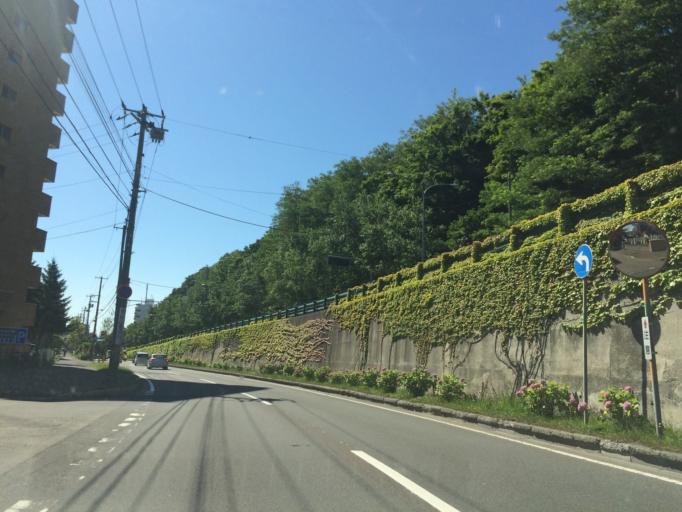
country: JP
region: Hokkaido
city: Sapporo
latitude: 43.0516
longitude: 141.3168
